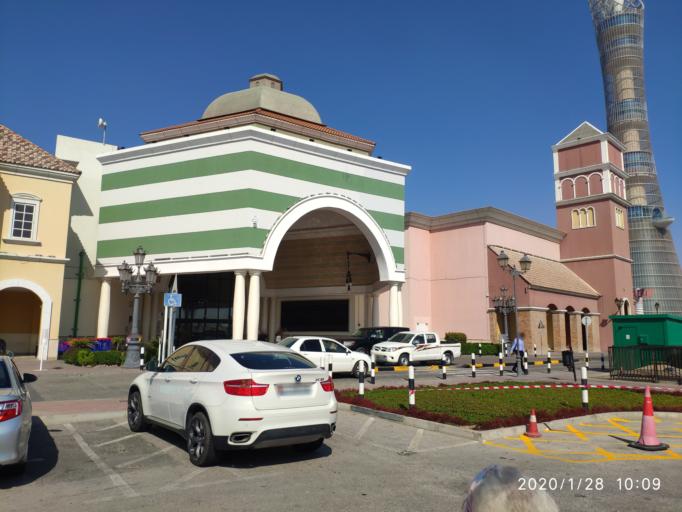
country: QA
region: Baladiyat ar Rayyan
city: Ar Rayyan
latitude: 25.2587
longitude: 51.4443
